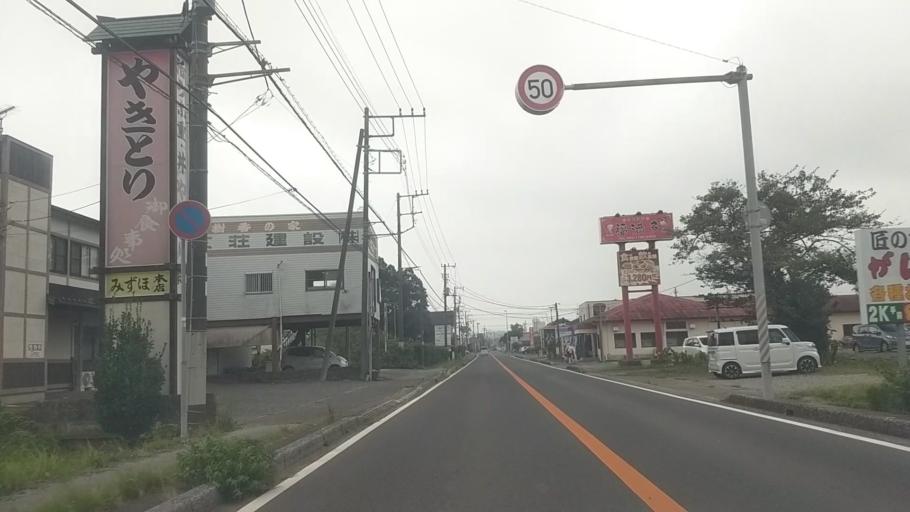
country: JP
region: Chiba
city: Ohara
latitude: 35.2396
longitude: 140.3914
